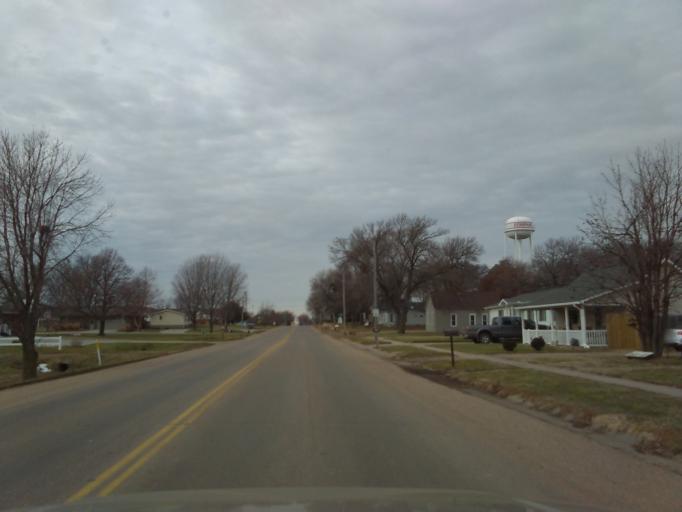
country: US
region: Nebraska
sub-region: Hall County
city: Grand Island
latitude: 40.7711
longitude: -98.3724
